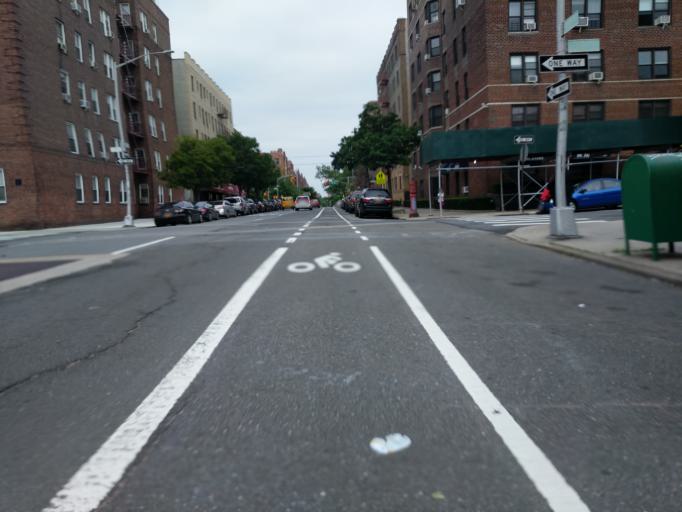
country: US
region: New York
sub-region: Queens County
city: Long Island City
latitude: 40.7457
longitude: -73.9251
